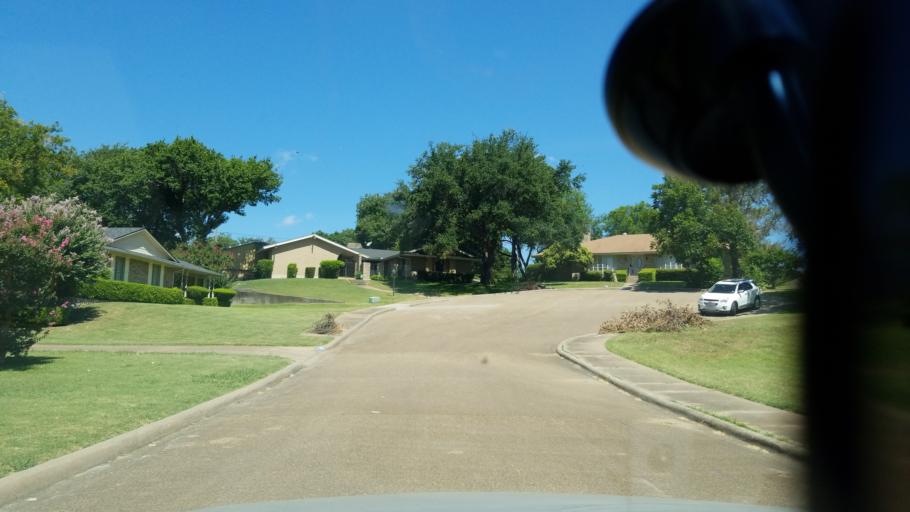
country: US
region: Texas
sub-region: Dallas County
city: Cockrell Hill
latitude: 32.6794
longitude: -96.8322
